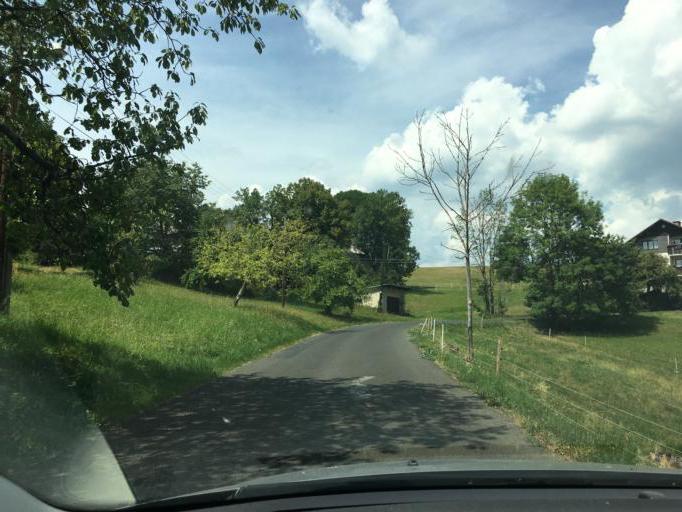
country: CZ
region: Liberecky
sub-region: Okres Semily
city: Ponikla
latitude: 50.6781
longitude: 15.4862
